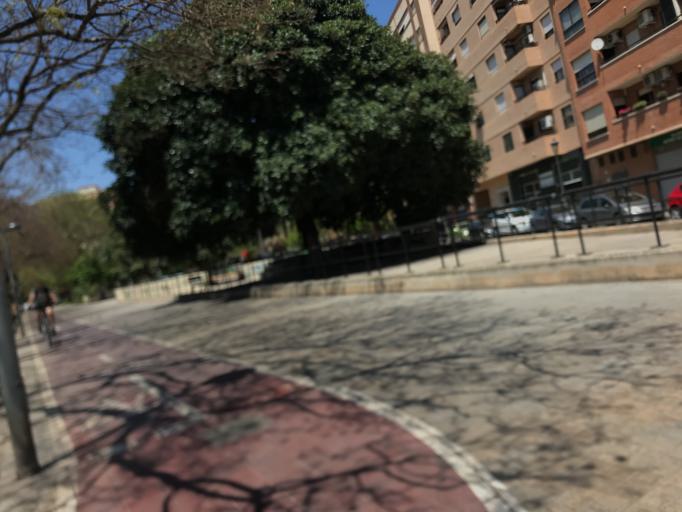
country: ES
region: Valencia
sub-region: Provincia de Valencia
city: Mislata
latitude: 39.4602
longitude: -0.4033
